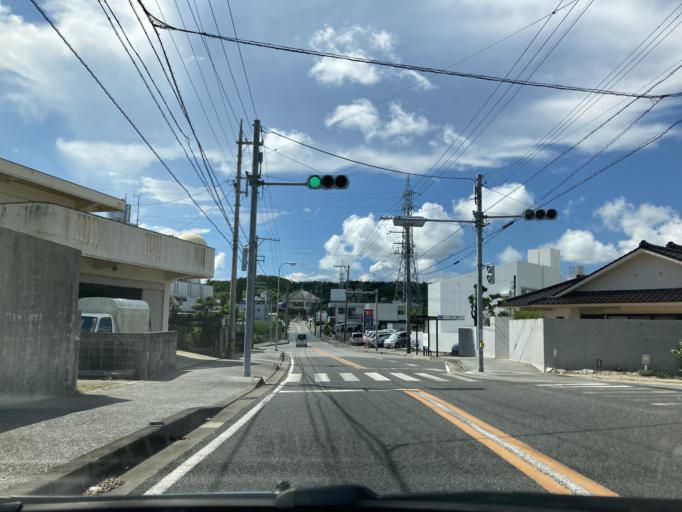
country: JP
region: Okinawa
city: Tomigusuku
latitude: 26.1689
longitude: 127.7206
